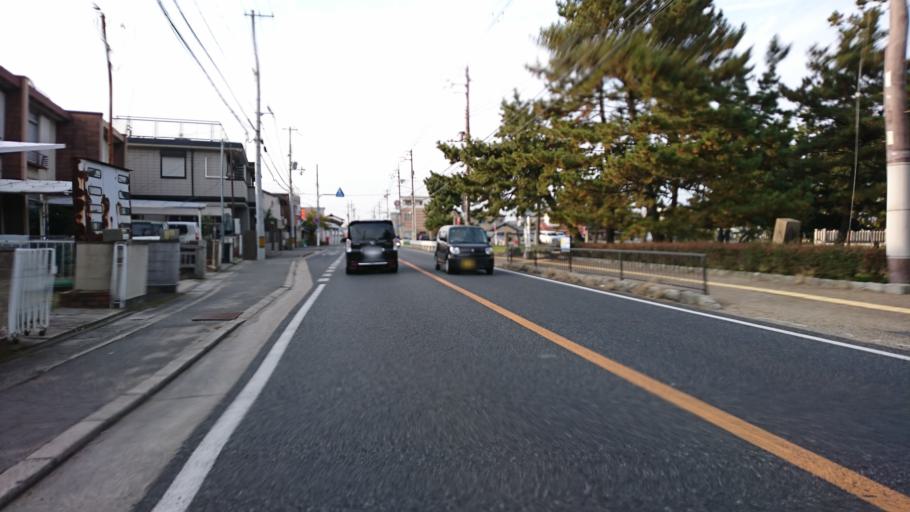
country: JP
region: Hyogo
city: Kakogawacho-honmachi
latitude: 34.7346
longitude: 134.8310
